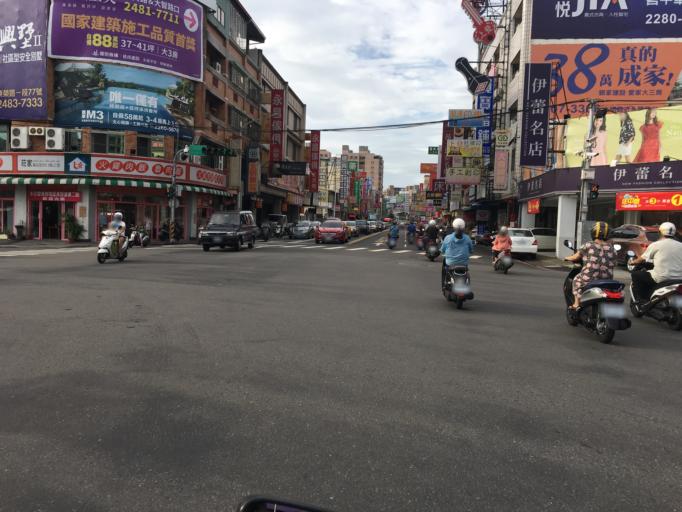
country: TW
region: Taiwan
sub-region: Taichung City
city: Taichung
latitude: 24.1017
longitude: 120.6883
